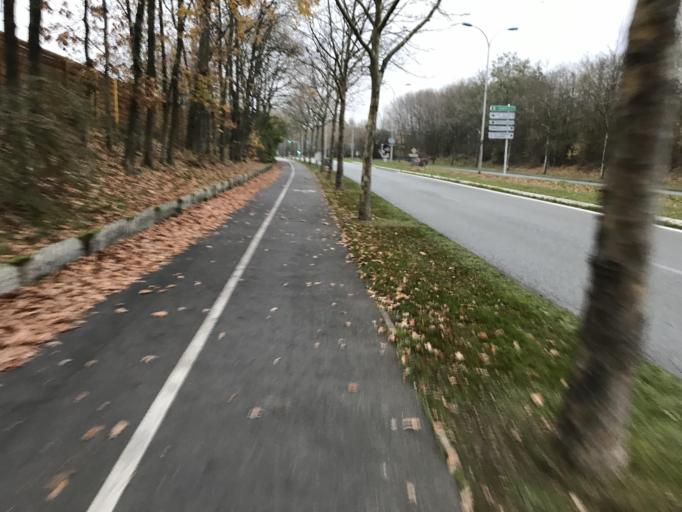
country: FR
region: Ile-de-France
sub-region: Departement des Yvelines
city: Saint-Quentin-en-Yvelines
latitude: 48.7666
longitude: 2.0103
